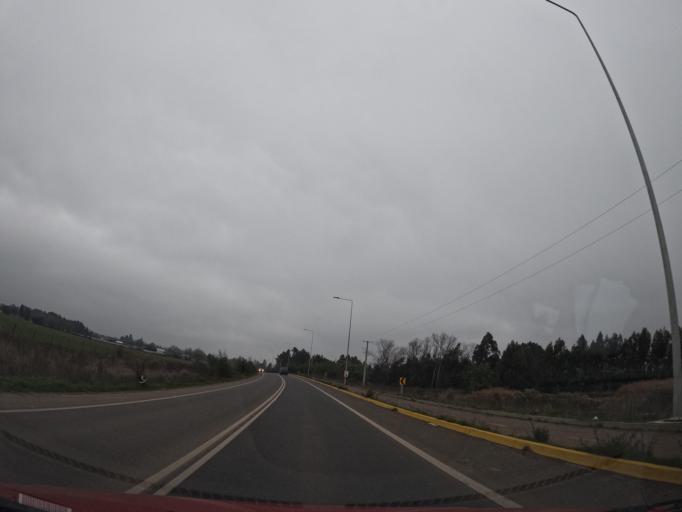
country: CL
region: Maule
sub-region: Provincia de Talca
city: San Clemente
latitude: -35.5442
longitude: -71.4737
